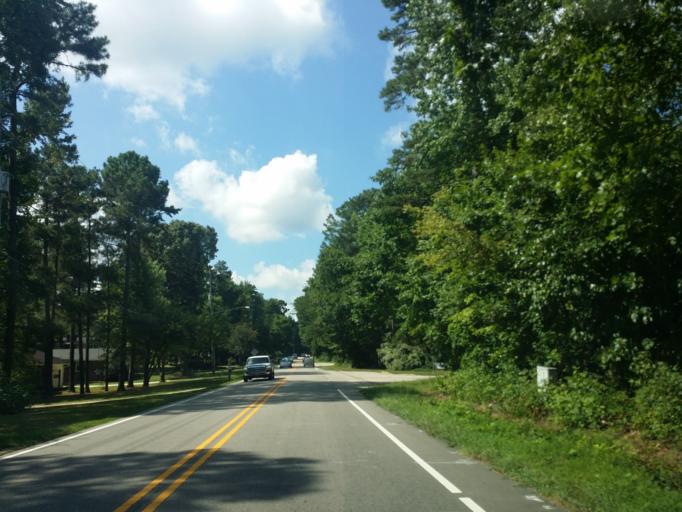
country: US
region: North Carolina
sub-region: Wake County
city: West Raleigh
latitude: 35.8799
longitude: -78.7071
